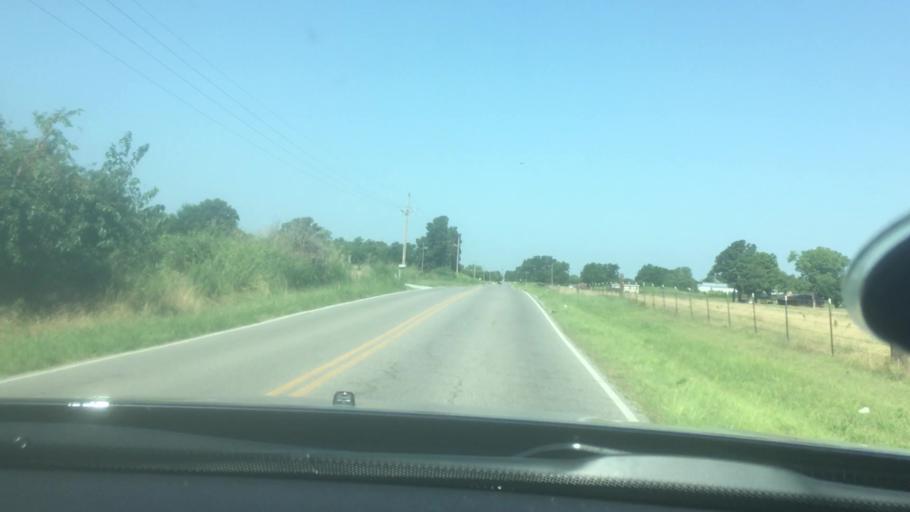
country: US
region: Oklahoma
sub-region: Bryan County
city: Calera
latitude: 34.0198
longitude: -96.4674
